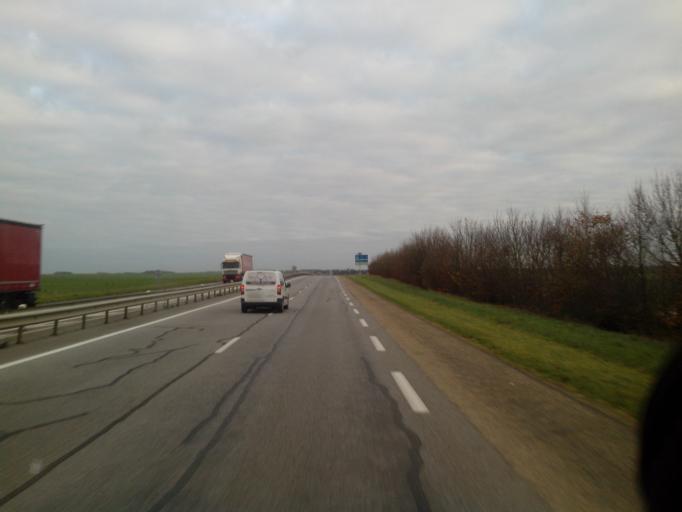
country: FR
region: Poitou-Charentes
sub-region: Departement de la Vienne
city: Vouille
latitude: 46.6513
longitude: 0.1345
